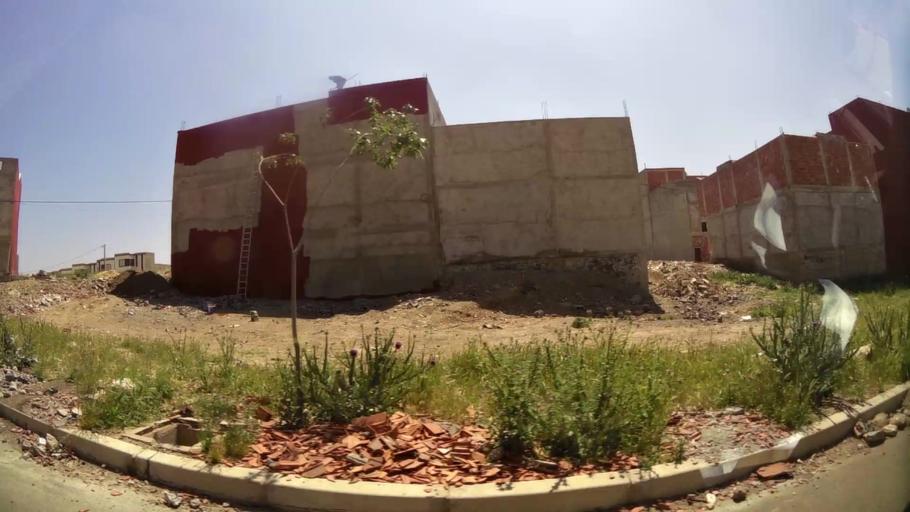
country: MA
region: Oriental
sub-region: Oujda-Angad
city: Oujda
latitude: 34.6729
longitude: -1.9466
